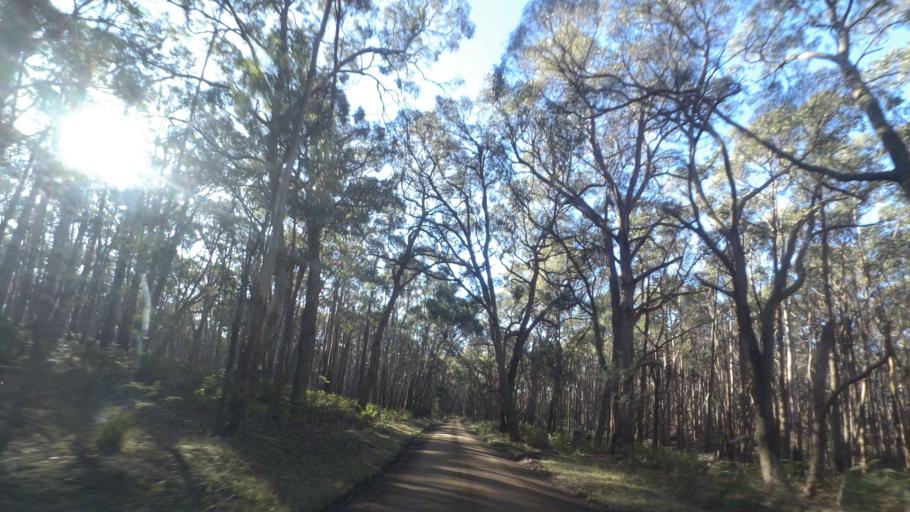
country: AU
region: Victoria
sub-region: Mount Alexander
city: Castlemaine
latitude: -37.2848
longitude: 144.3323
